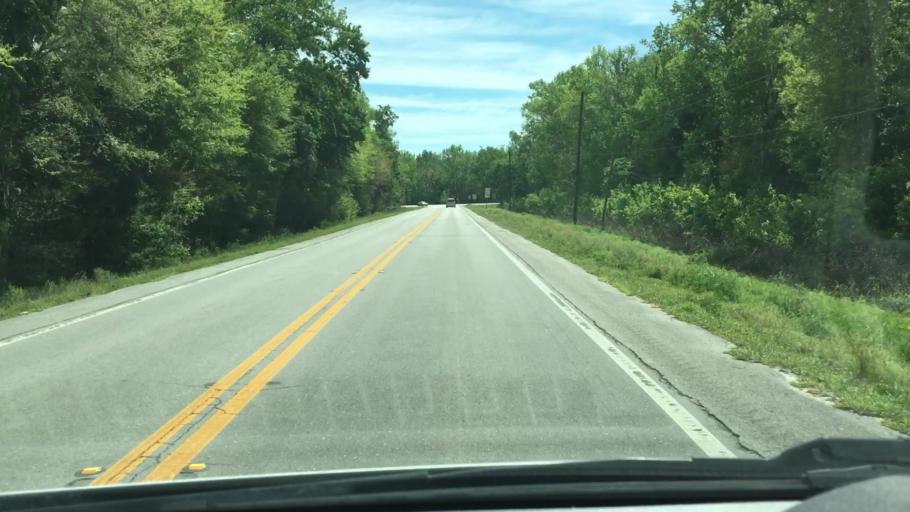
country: US
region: Florida
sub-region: Lake County
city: Lake Mack-Forest Hills
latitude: 29.0069
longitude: -81.3880
